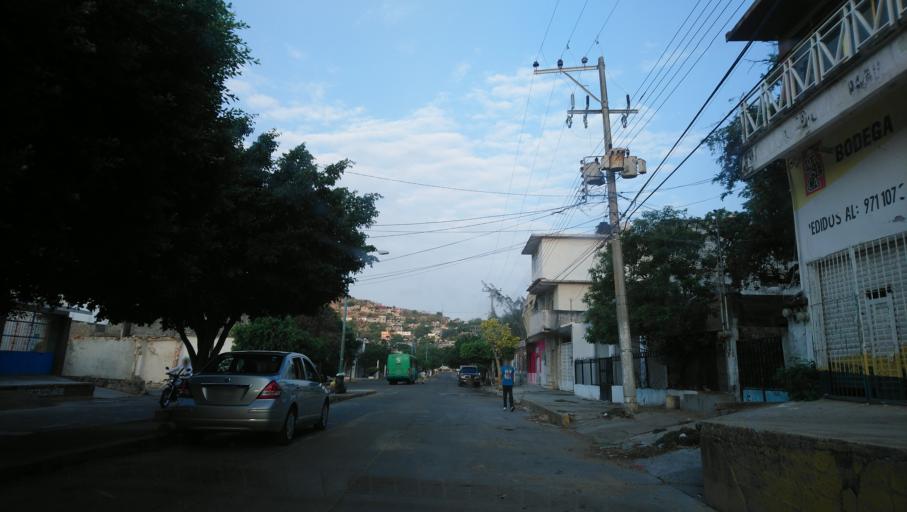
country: MX
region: Oaxaca
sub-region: Salina Cruz
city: Salina Cruz
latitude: 16.1839
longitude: -95.1974
